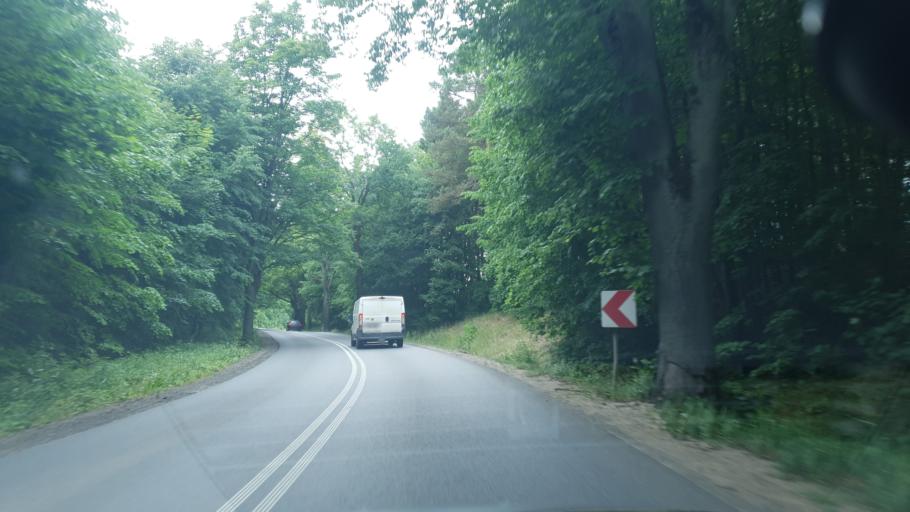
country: PL
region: Pomeranian Voivodeship
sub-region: Powiat kartuski
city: Zukowo
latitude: 54.3863
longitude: 18.3391
